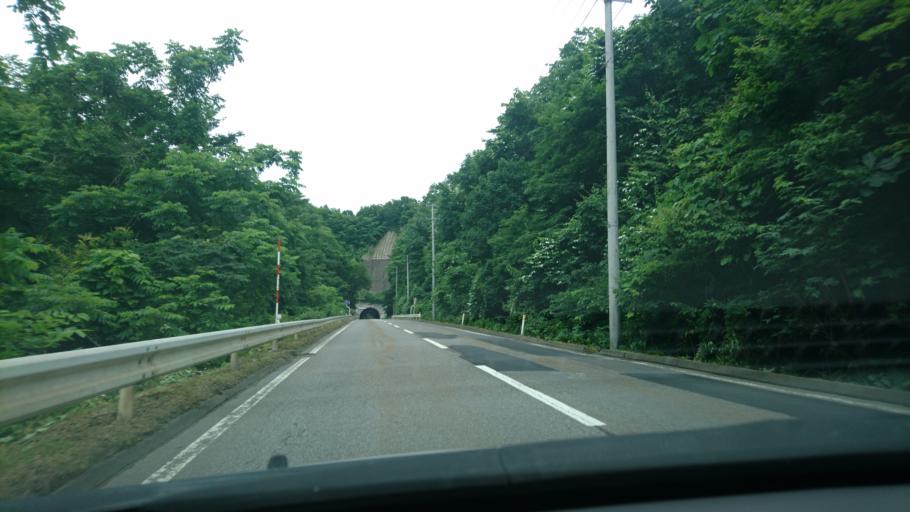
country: JP
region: Iwate
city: Miyako
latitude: 39.9685
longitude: 141.8604
